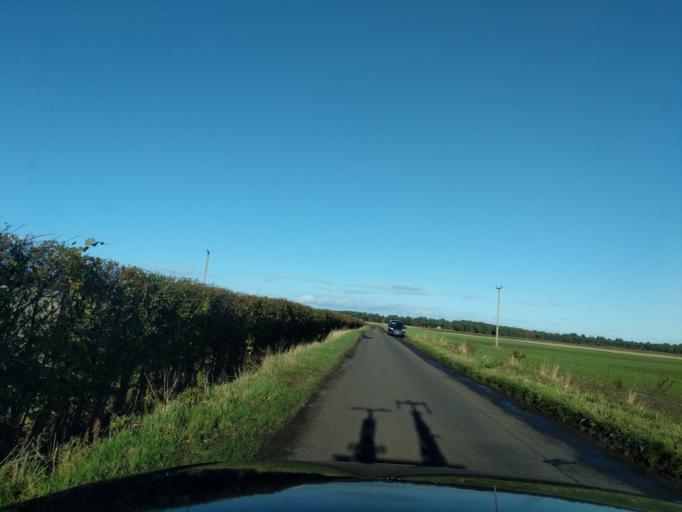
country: GB
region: Scotland
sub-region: Fife
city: Leuchars
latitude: 56.3952
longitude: -2.8686
